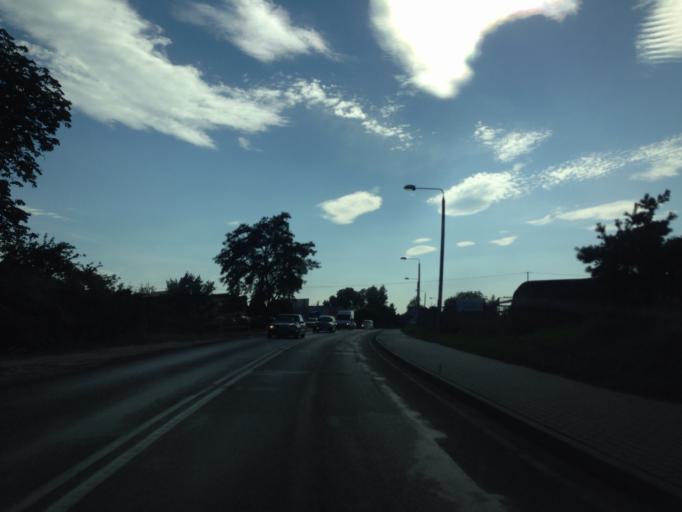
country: PL
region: Kujawsko-Pomorskie
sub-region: Powiat aleksandrowski
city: Aleksandrow Kujawski
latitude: 52.8643
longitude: 18.7316
